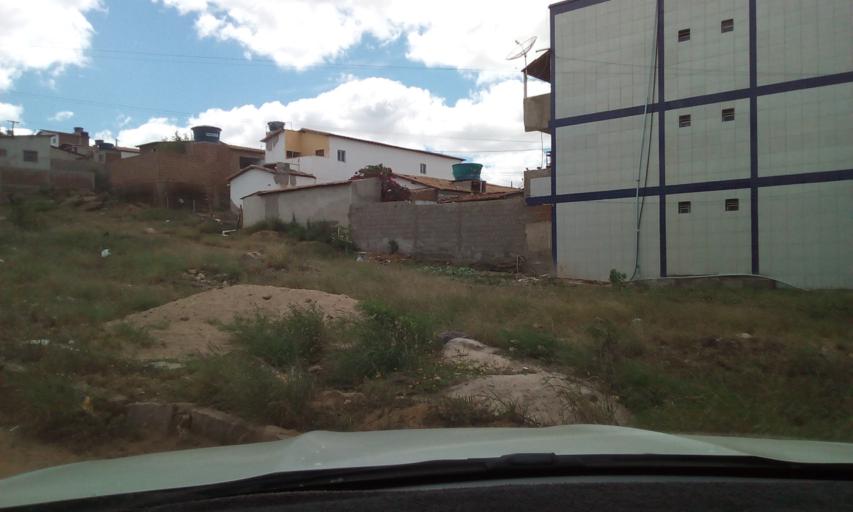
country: BR
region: Paraiba
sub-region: Picui
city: Picui
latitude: -6.5130
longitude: -36.3530
